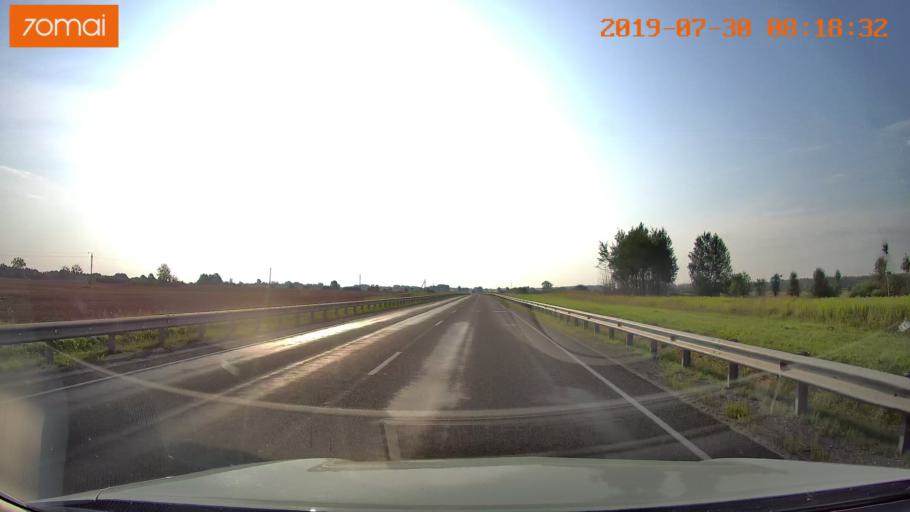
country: RU
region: Kaliningrad
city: Zheleznodorozhnyy
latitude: 54.6320
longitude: 21.4667
